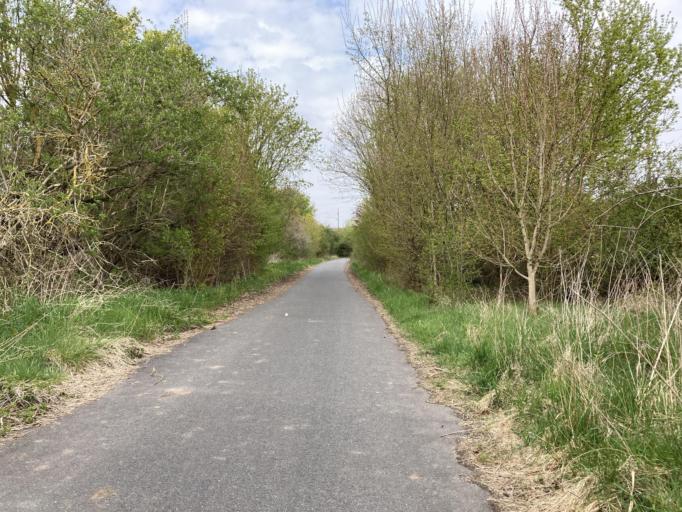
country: DE
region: Lower Saxony
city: Laatzen
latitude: 52.2755
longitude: 9.8261
